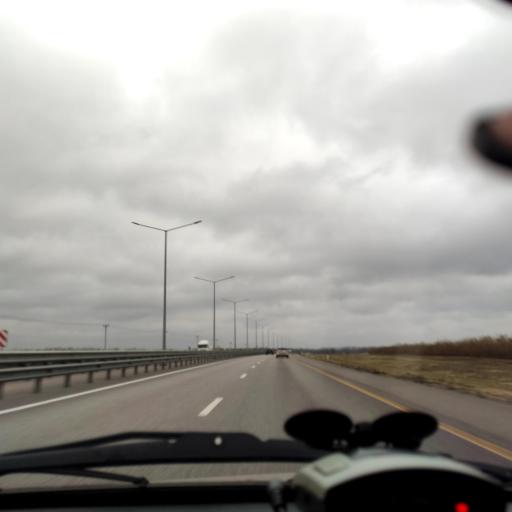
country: RU
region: Voronezj
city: Podkletnoye
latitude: 51.5874
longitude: 39.4444
